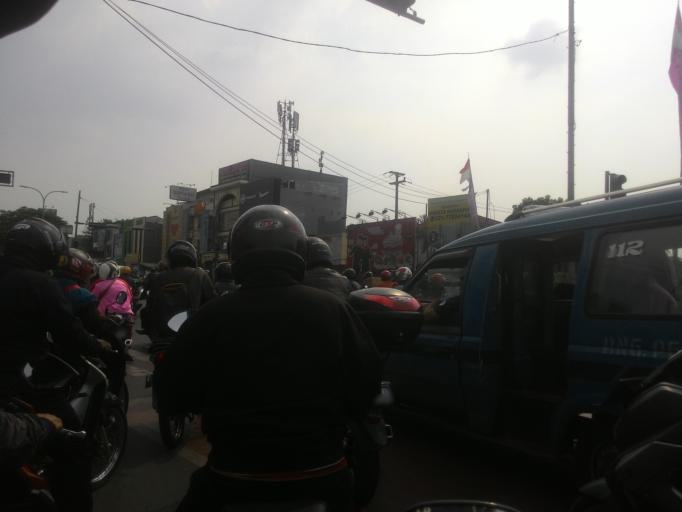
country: ID
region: West Java
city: Depok
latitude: -6.3765
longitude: 106.8321
